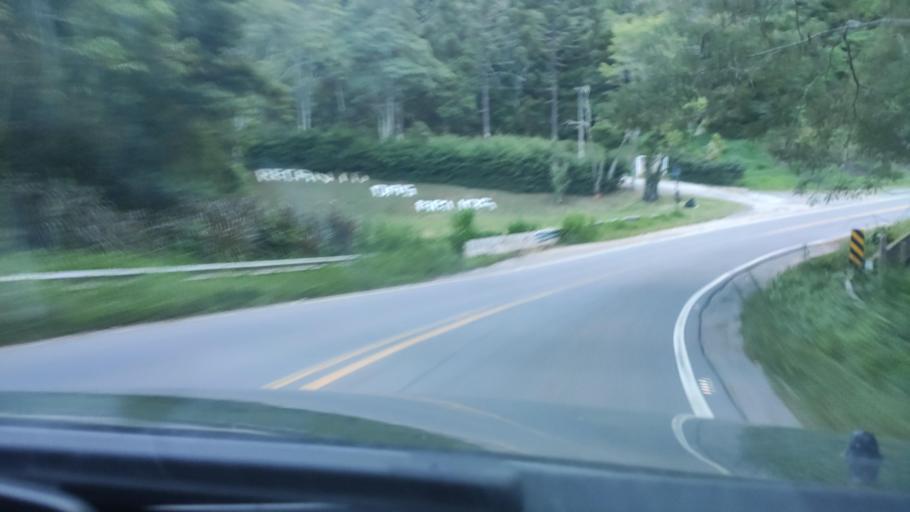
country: BR
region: Sao Paulo
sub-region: Campos Do Jordao
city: Campos do Jordao
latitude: -22.8301
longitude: -45.6939
